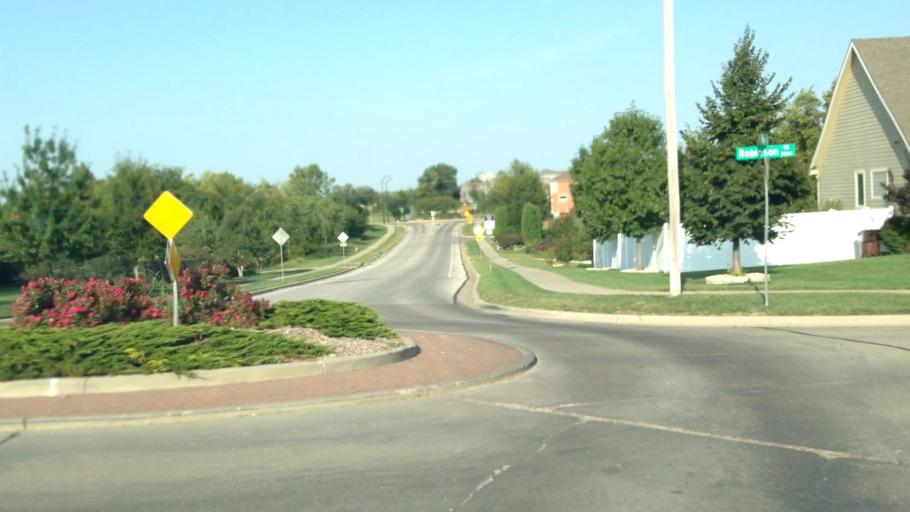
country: US
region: Kansas
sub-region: Douglas County
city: Lawrence
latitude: 38.9643
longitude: -95.3230
